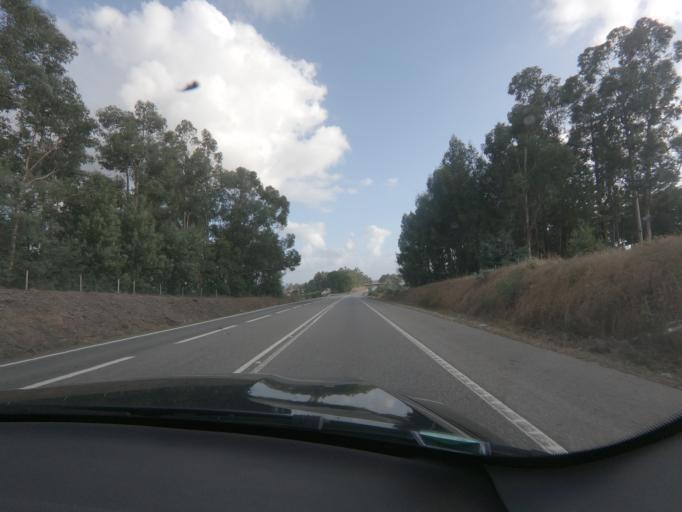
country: PT
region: Viseu
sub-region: Concelho de Tondela
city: Tondela
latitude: 40.5529
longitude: -8.0525
